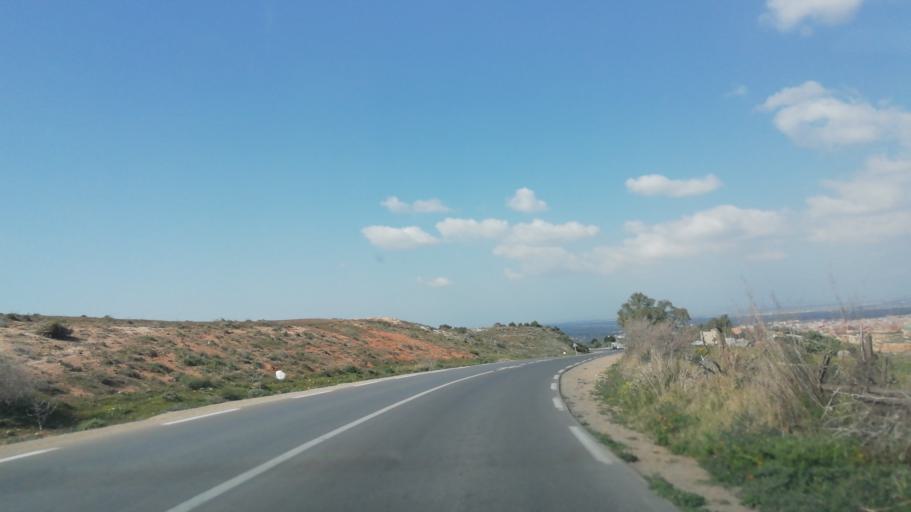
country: DZ
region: Mascara
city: Mascara
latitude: 35.5555
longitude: 0.0786
